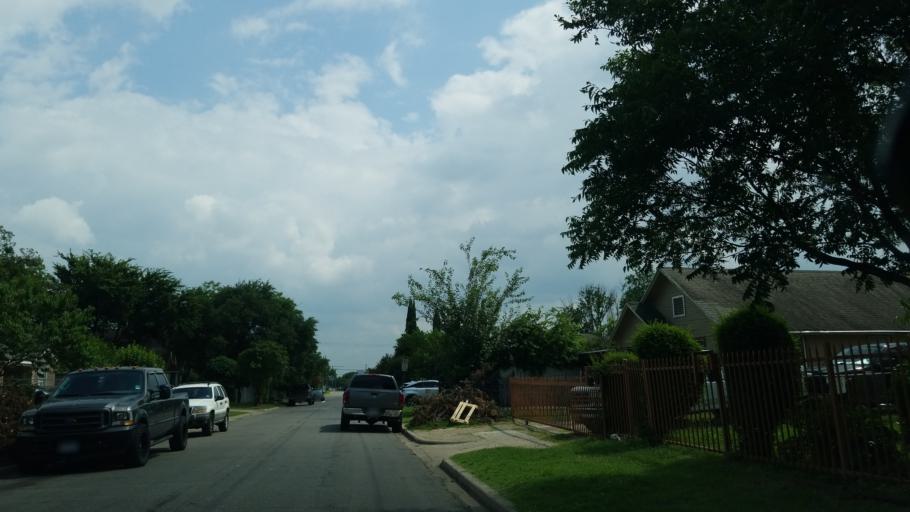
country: US
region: Texas
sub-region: Dallas County
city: University Park
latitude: 32.8395
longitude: -96.8312
